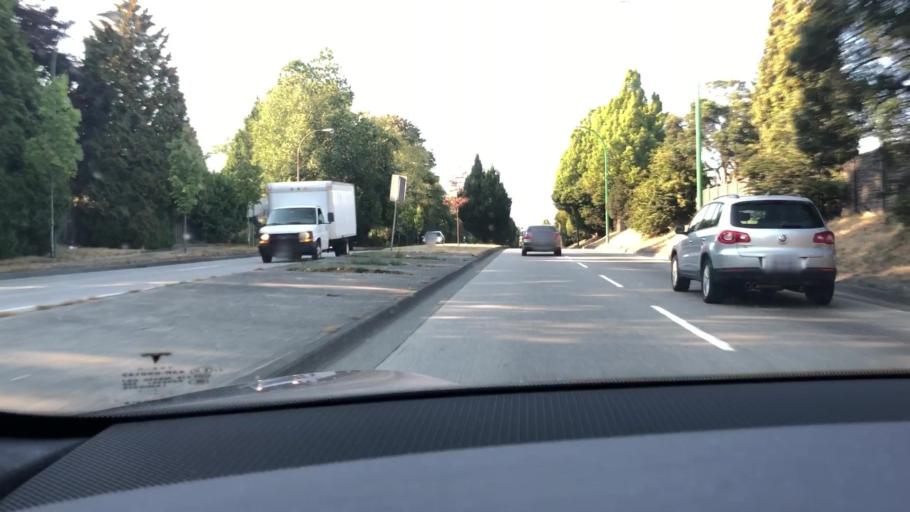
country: CA
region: British Columbia
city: Burnaby
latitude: 49.2156
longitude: -123.0237
